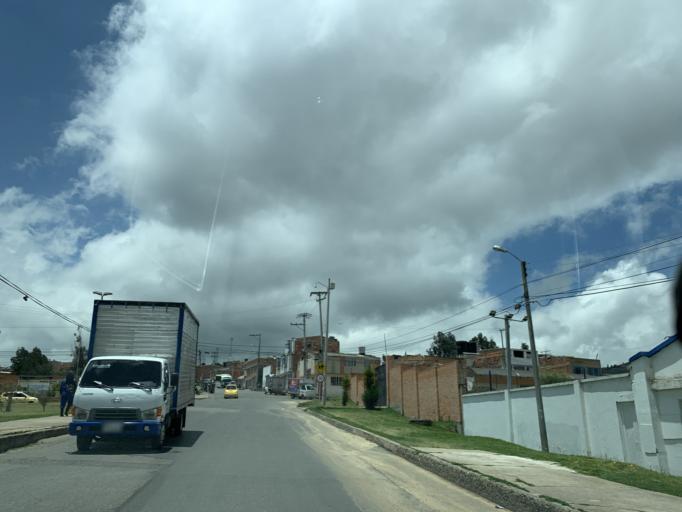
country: CO
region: Boyaca
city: Tunja
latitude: 5.5200
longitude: -73.3567
